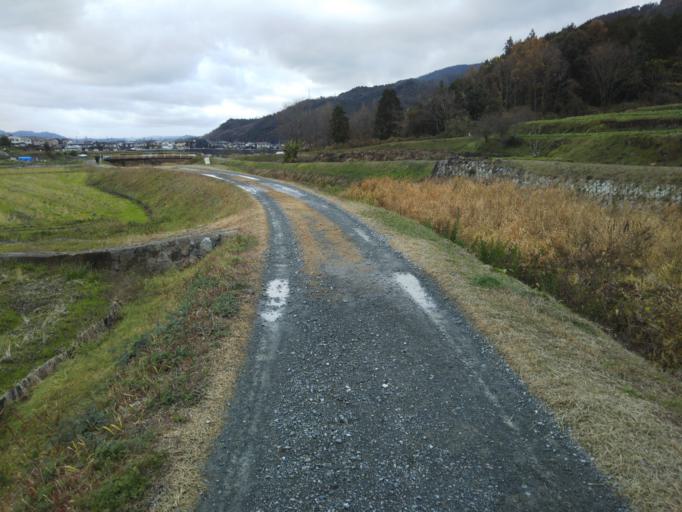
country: JP
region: Kyoto
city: Kameoka
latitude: 35.0048
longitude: 135.6143
